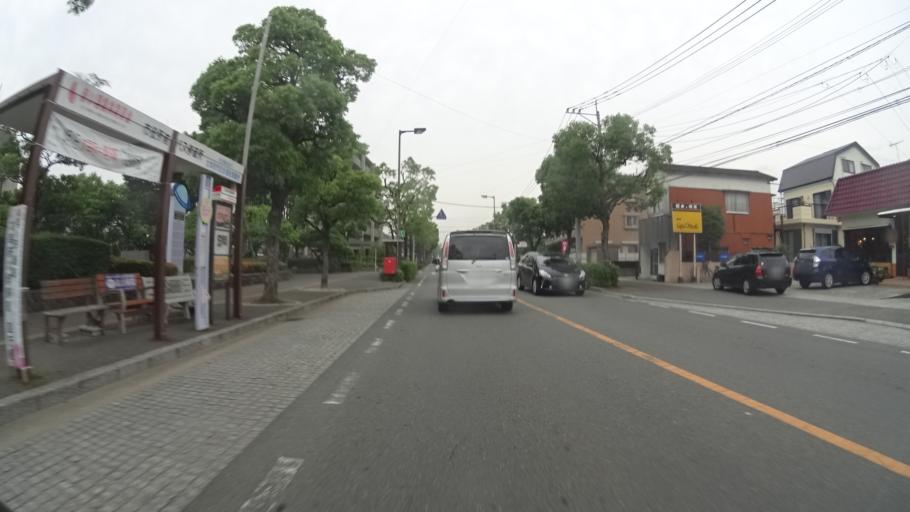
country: JP
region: Fukuoka
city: Dazaifu
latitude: 33.5135
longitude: 130.5241
